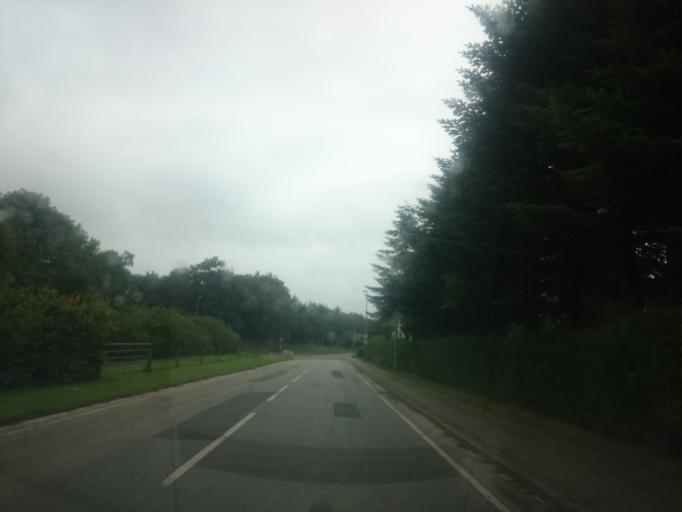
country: DK
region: South Denmark
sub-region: Vejen Kommune
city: Holsted
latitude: 55.5985
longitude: 8.8028
